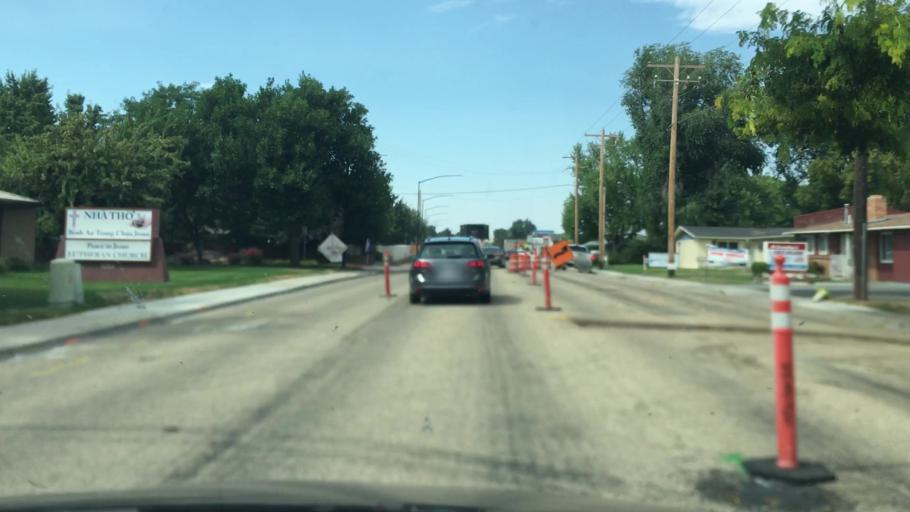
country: US
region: Idaho
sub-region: Ada County
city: Garden City
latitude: 43.6159
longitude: -116.2742
